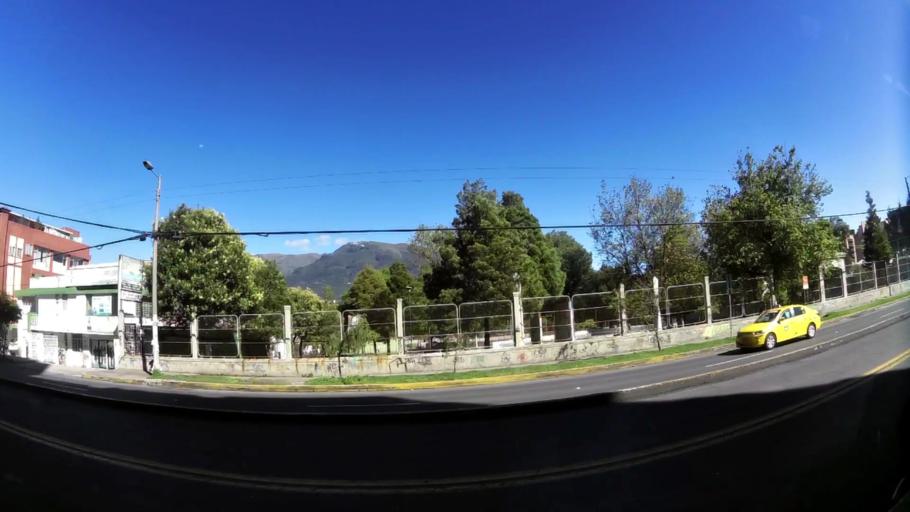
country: EC
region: Pichincha
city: Quito
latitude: -0.1727
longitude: -78.4769
